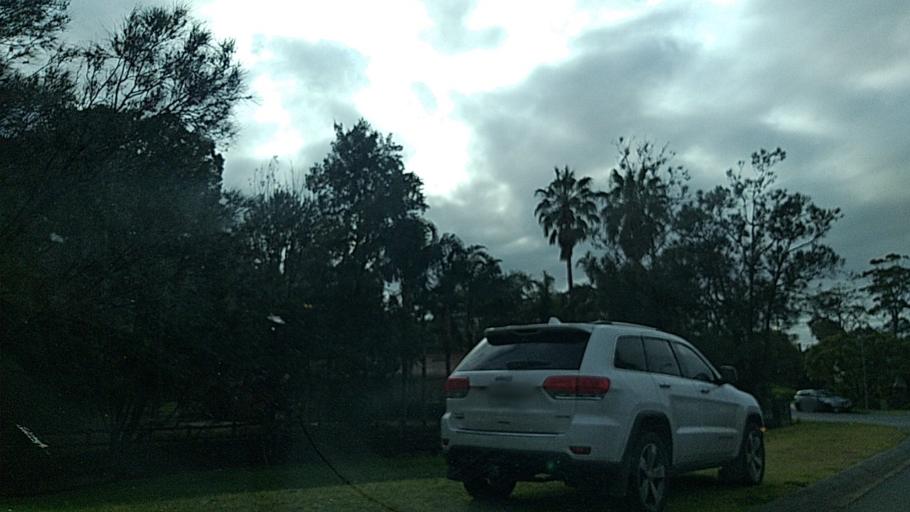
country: AU
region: New South Wales
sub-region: Wollongong
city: Bulli
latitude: -34.3259
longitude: 150.9087
